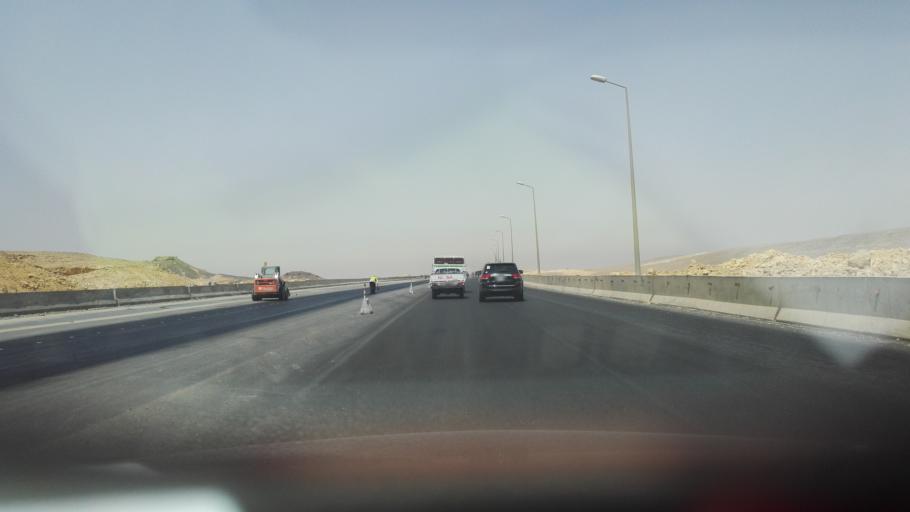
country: EG
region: As Suways
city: Ain Sukhna
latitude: 29.6992
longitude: 32.1015
